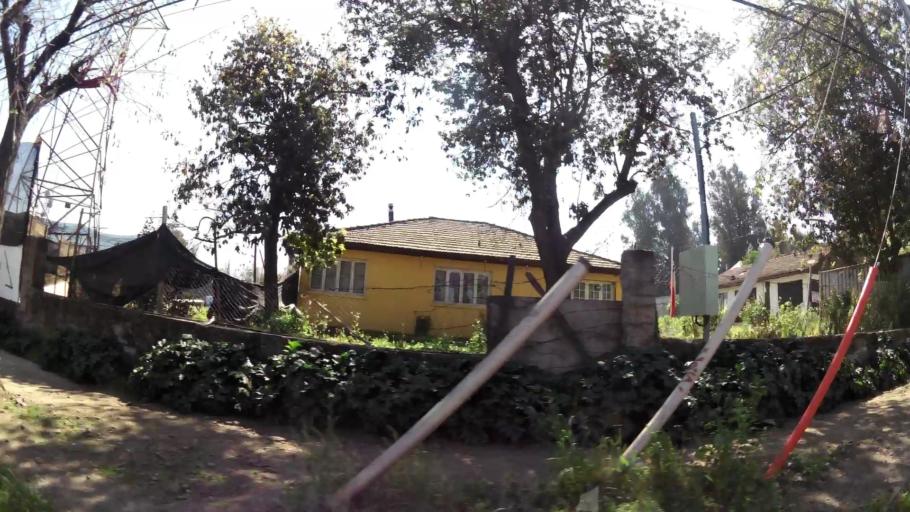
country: CL
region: Santiago Metropolitan
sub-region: Provincia de Santiago
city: Villa Presidente Frei, Nunoa, Santiago, Chile
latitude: -33.4410
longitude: -70.5321
